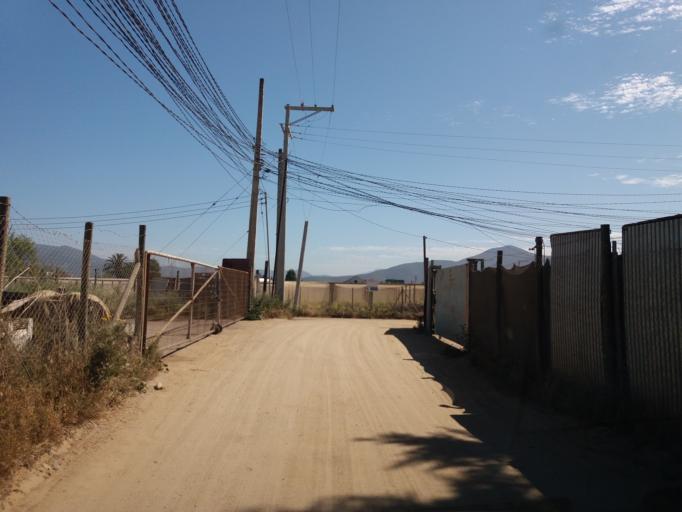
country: CL
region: Valparaiso
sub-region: Provincia de Quillota
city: Quillota
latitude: -32.8750
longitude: -71.2251
